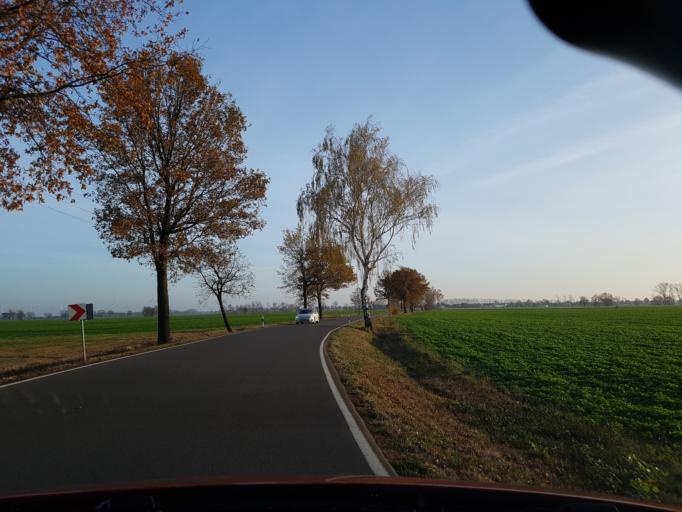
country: DE
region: Brandenburg
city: Bad Liebenwerda
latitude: 51.4728
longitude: 13.4246
